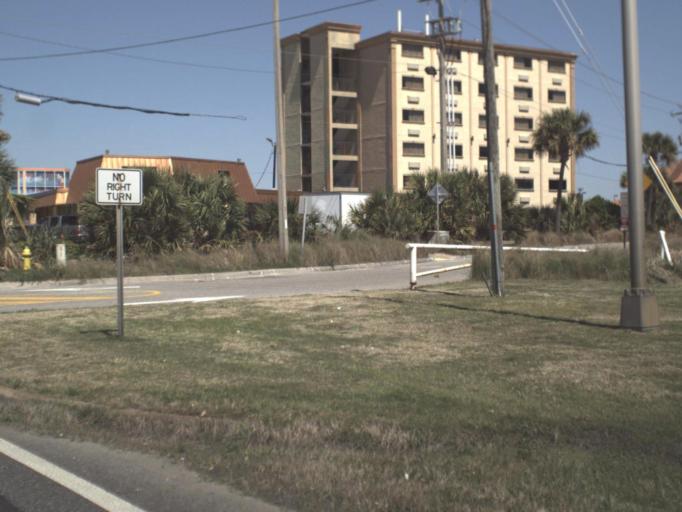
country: US
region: Florida
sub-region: Okaloosa County
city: Fort Walton Beach
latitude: 30.3967
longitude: -86.5956
